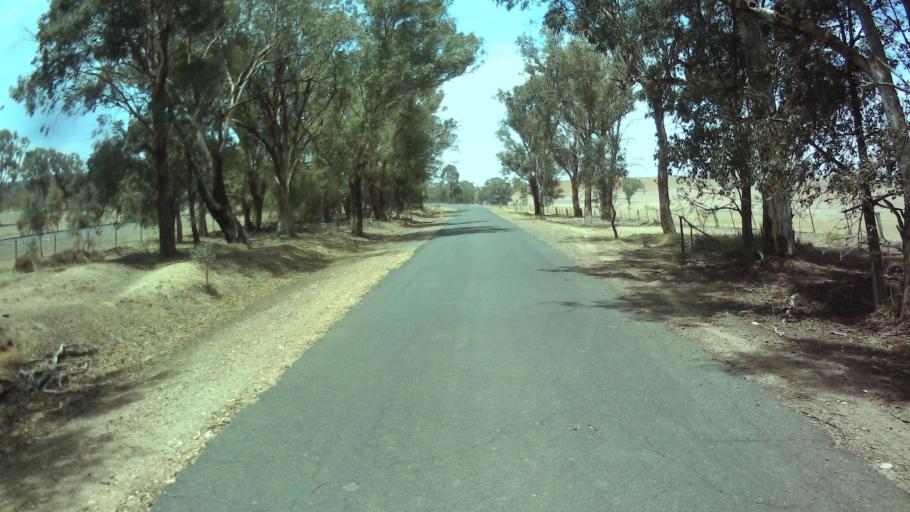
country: AU
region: New South Wales
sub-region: Weddin
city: Grenfell
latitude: -34.0213
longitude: 148.4327
